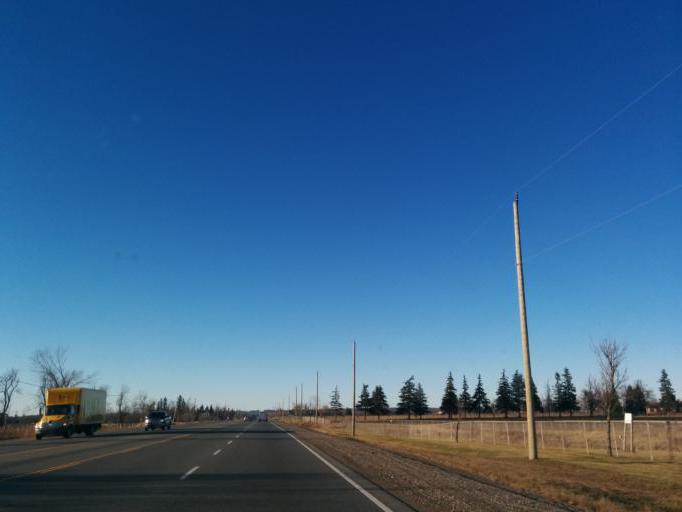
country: CA
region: Ontario
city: Brampton
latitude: 43.7778
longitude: -79.8840
